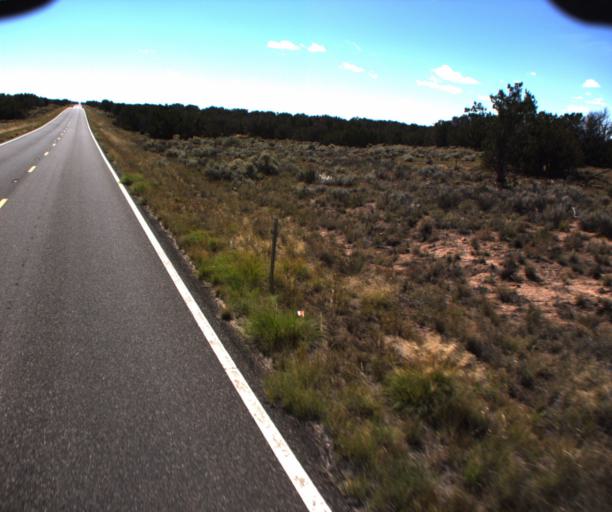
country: US
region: Arizona
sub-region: Apache County
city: Houck
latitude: 34.8912
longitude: -109.2380
